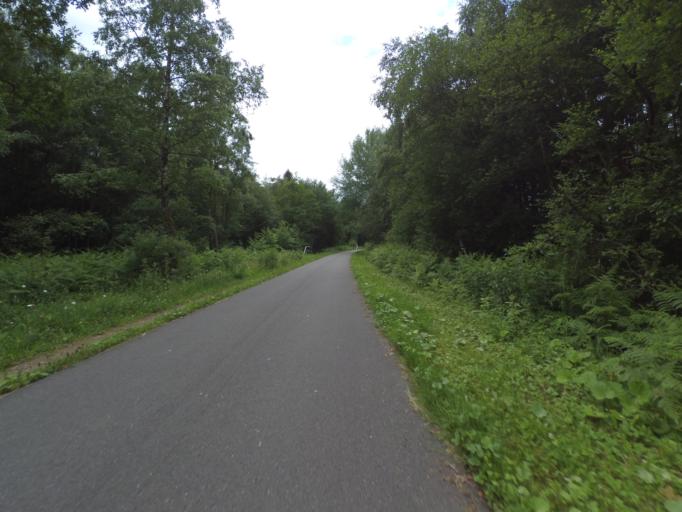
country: DE
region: North Rhine-Westphalia
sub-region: Regierungsbezirk Koln
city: Roetgen
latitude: 50.6411
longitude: 6.2233
